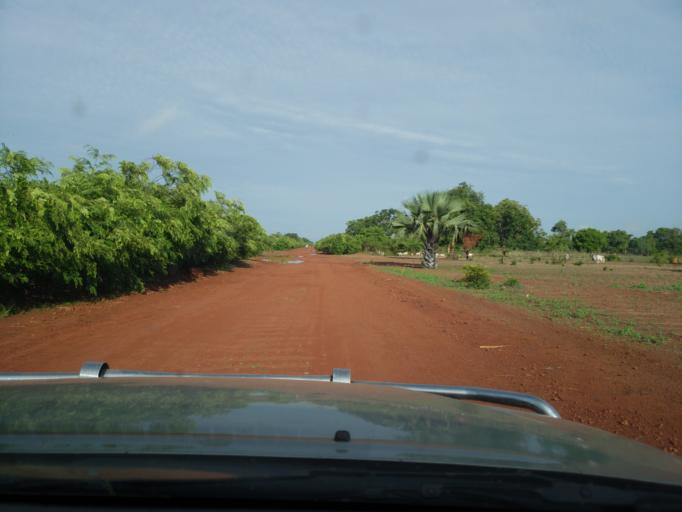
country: ML
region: Sikasso
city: Koutiala
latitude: 12.4180
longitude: -5.7086
